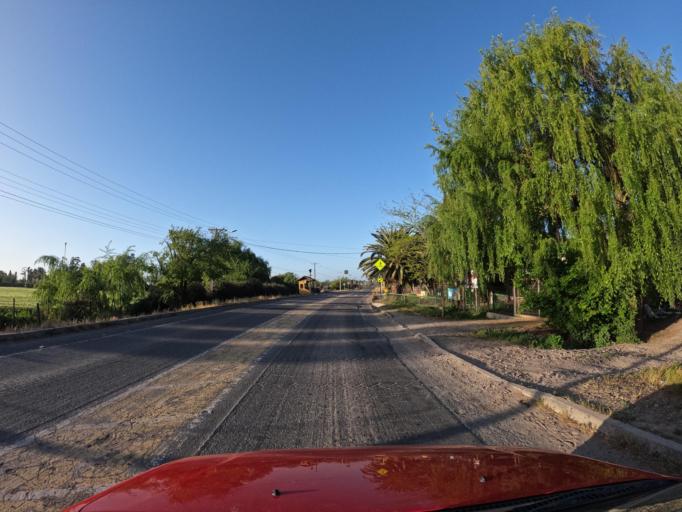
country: CL
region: O'Higgins
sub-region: Provincia de Colchagua
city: Santa Cruz
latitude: -34.3580
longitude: -71.4123
